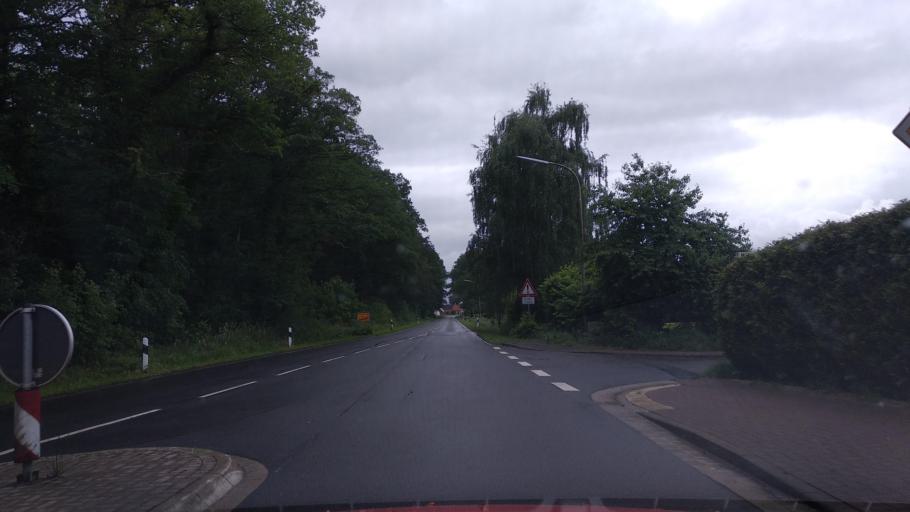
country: DE
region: Lower Saxony
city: Auhagen
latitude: 52.3908
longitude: 9.2819
